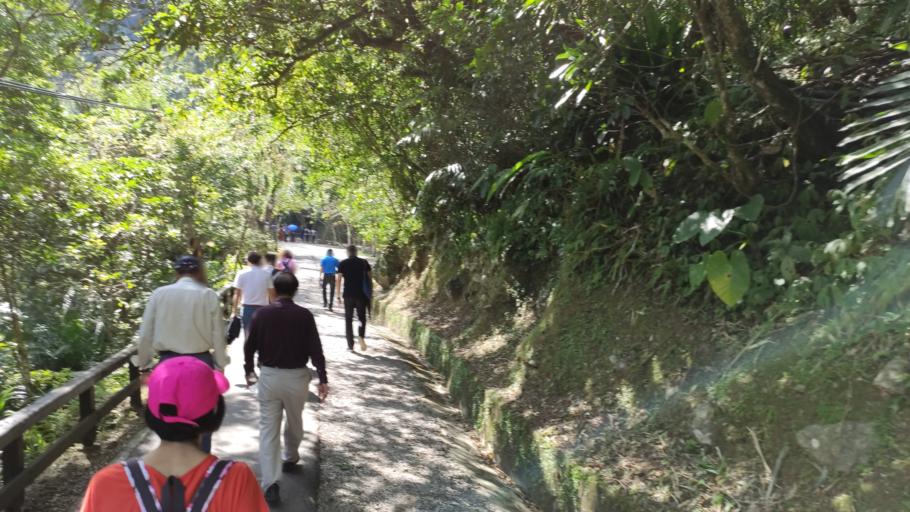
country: TW
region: Taiwan
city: Daxi
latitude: 24.8300
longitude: 121.4446
